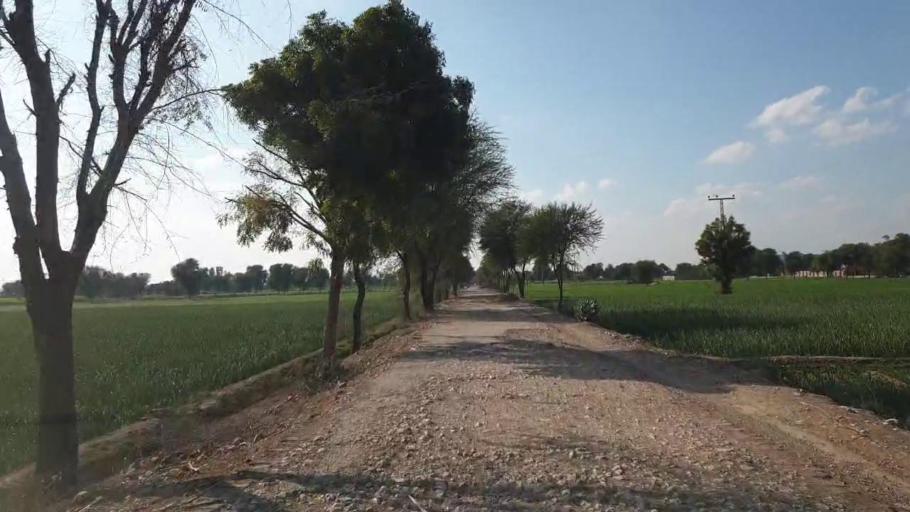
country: PK
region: Sindh
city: Shahpur Chakar
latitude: 26.1095
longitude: 68.5617
